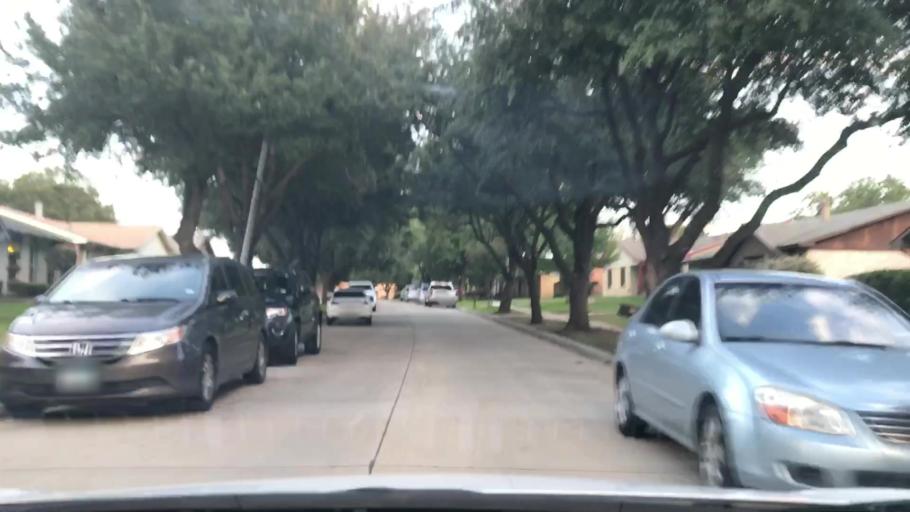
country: US
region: Texas
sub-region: Dallas County
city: Carrollton
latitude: 33.0064
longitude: -96.8764
